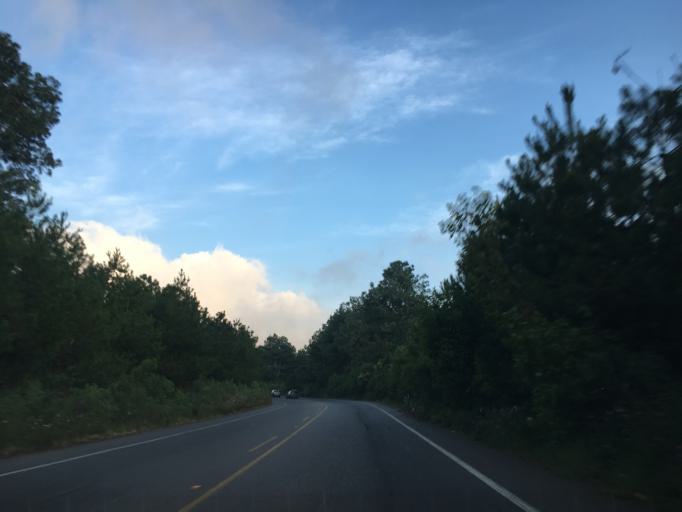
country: MX
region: Michoacan
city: Angahuan
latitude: 19.5686
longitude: -102.2541
